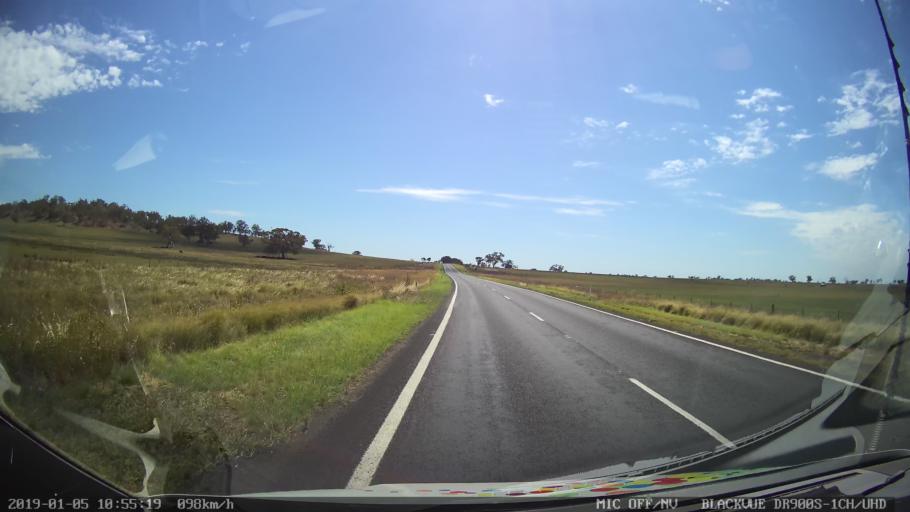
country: AU
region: New South Wales
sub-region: Warrumbungle Shire
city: Coonabarabran
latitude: -31.4489
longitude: 149.1419
